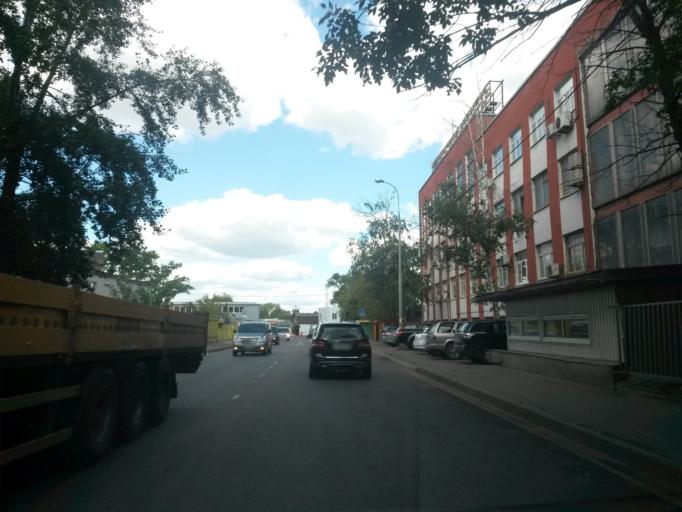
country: RU
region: Moscow
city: Tekstil'shchiki
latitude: 55.7029
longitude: 37.7082
